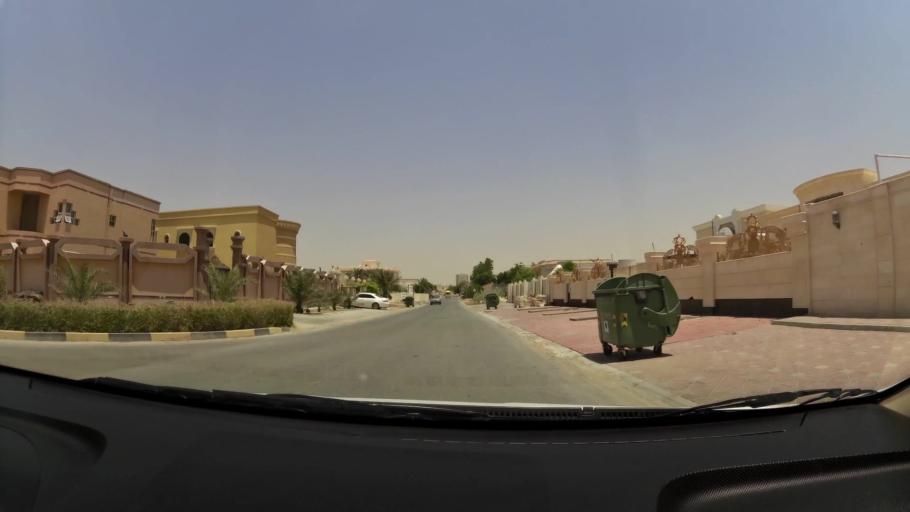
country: AE
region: Ajman
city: Ajman
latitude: 25.4105
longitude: 55.4982
